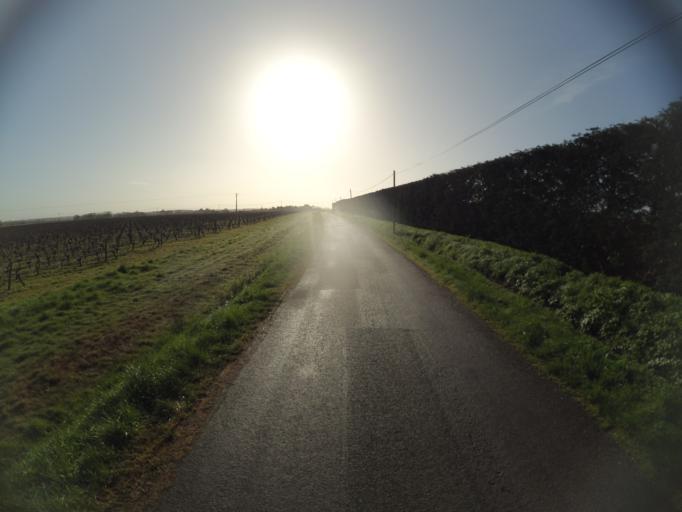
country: FR
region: Pays de la Loire
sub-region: Departement de la Loire-Atlantique
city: Remouille
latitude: 47.0485
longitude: -1.3924
